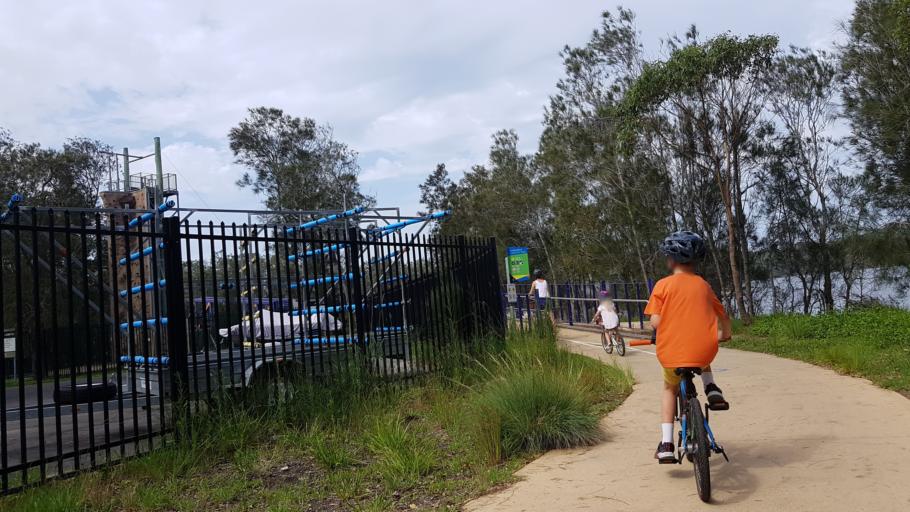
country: AU
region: New South Wales
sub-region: Pittwater
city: North Narrabeen
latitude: -33.7195
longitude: 151.2715
